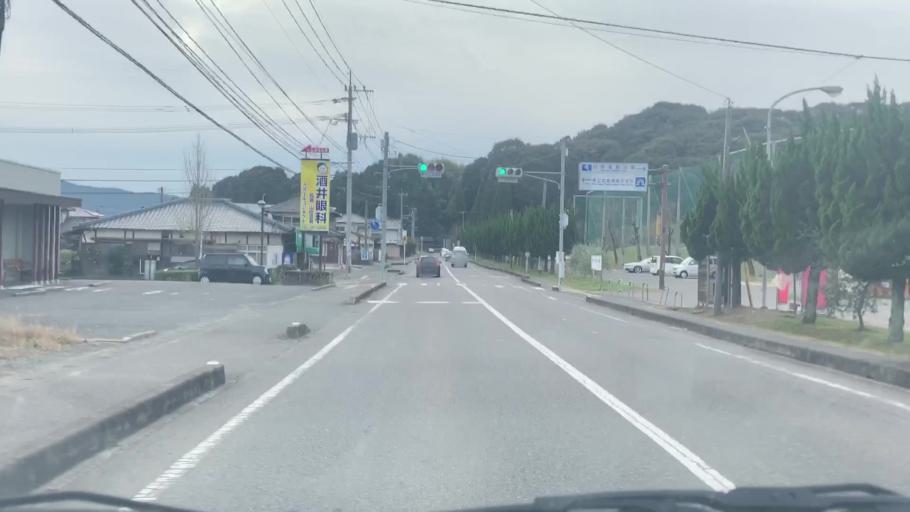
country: JP
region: Saga Prefecture
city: Takeocho-takeo
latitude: 33.1934
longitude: 130.0308
